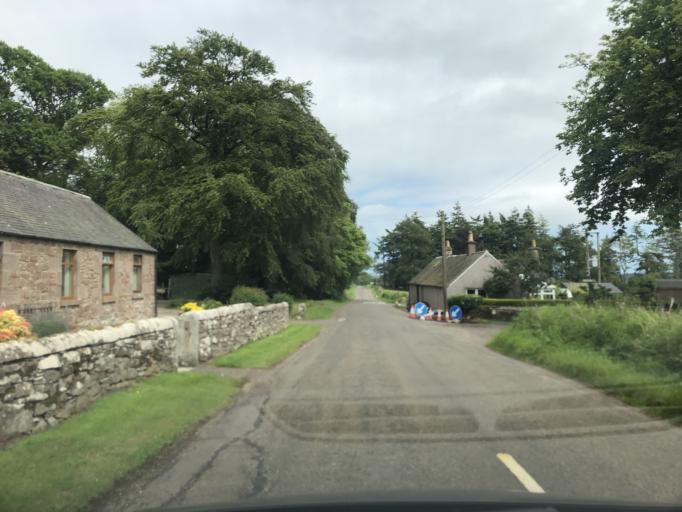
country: GB
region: Scotland
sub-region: Angus
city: Brechin
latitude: 56.7372
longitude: -2.7149
